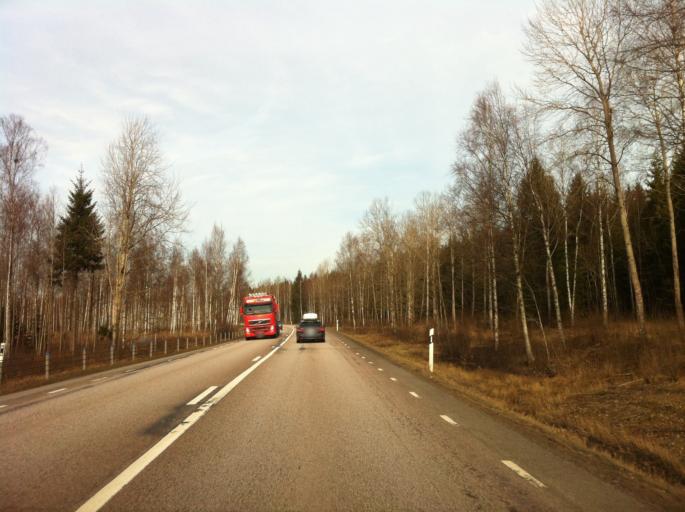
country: SE
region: Vaestra Goetaland
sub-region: Gullspangs Kommun
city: Gullspang
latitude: 59.0147
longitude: 14.1170
